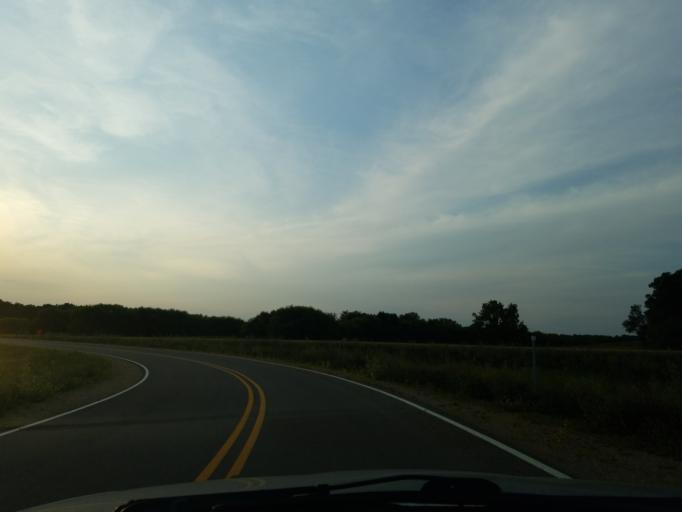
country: US
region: Minnesota
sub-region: Washington County
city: Stillwater
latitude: 45.0715
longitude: -92.7611
